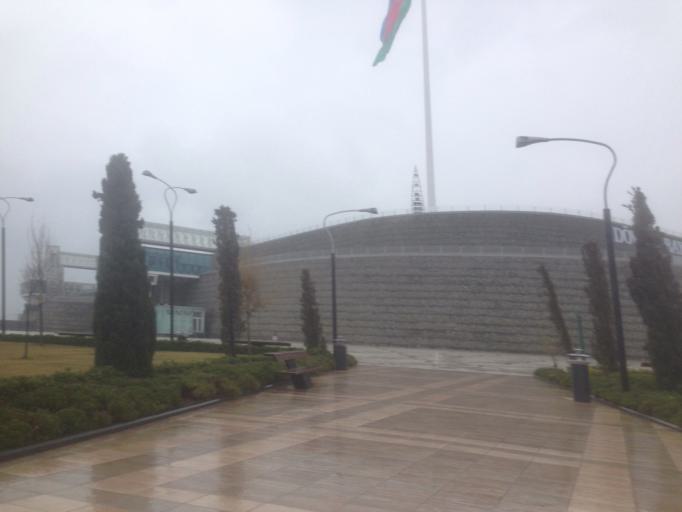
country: AZ
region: Baki
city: Badamdar
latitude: 40.3463
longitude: 49.8456
